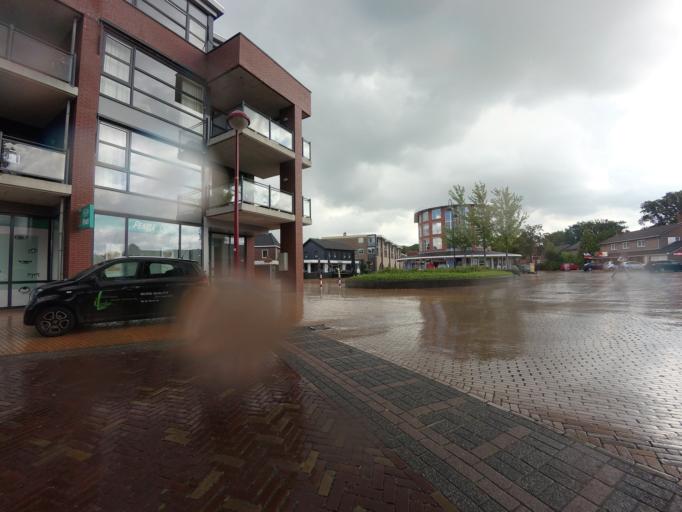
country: NL
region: Friesland
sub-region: Gemeente Heerenveen
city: Jubbega
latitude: 52.9892
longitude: 6.2903
